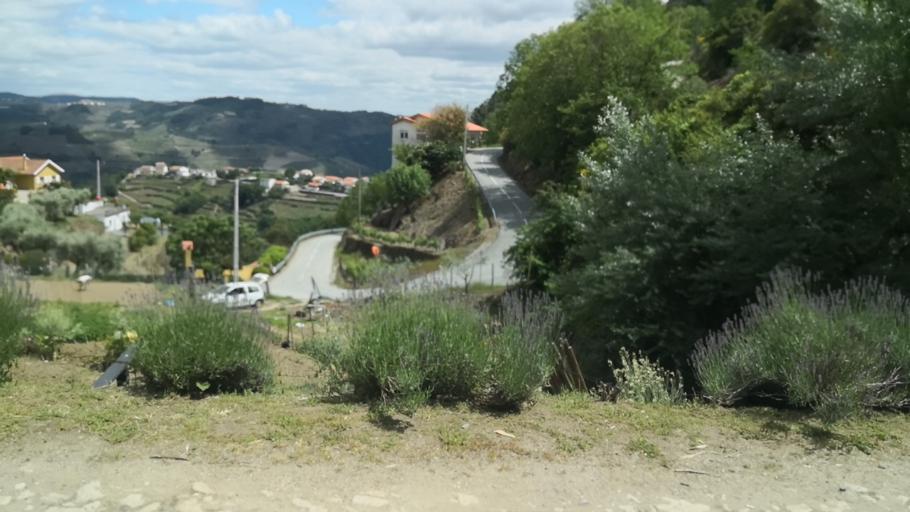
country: PT
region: Vila Real
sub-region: Santa Marta de Penaguiao
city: Santa Marta de Penaguiao
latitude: 41.2321
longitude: -7.7970
